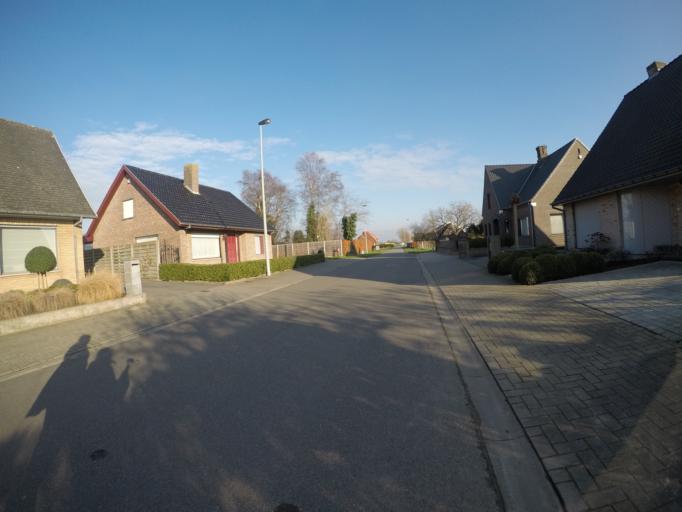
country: BE
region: Flanders
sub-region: Provincie West-Vlaanderen
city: Lichtervelde
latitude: 51.0792
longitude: 3.1728
